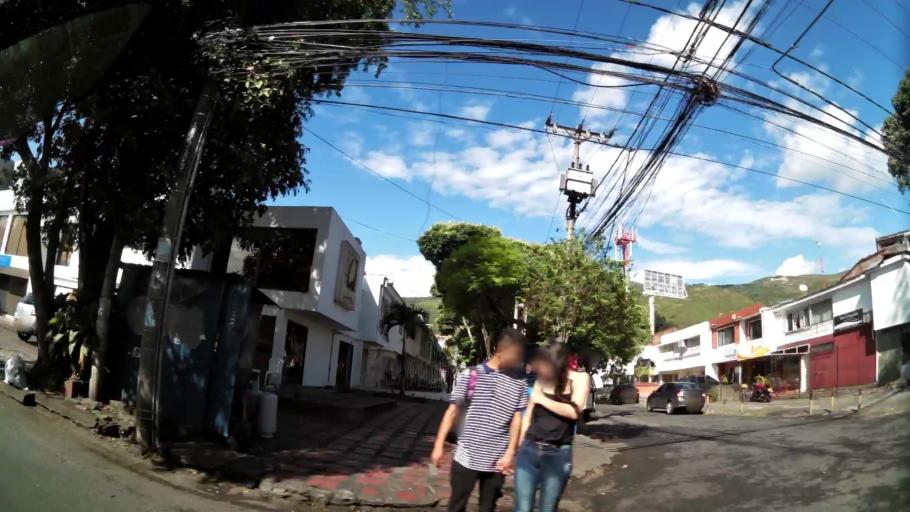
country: CO
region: Valle del Cauca
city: Cali
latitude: 3.4683
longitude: -76.5281
